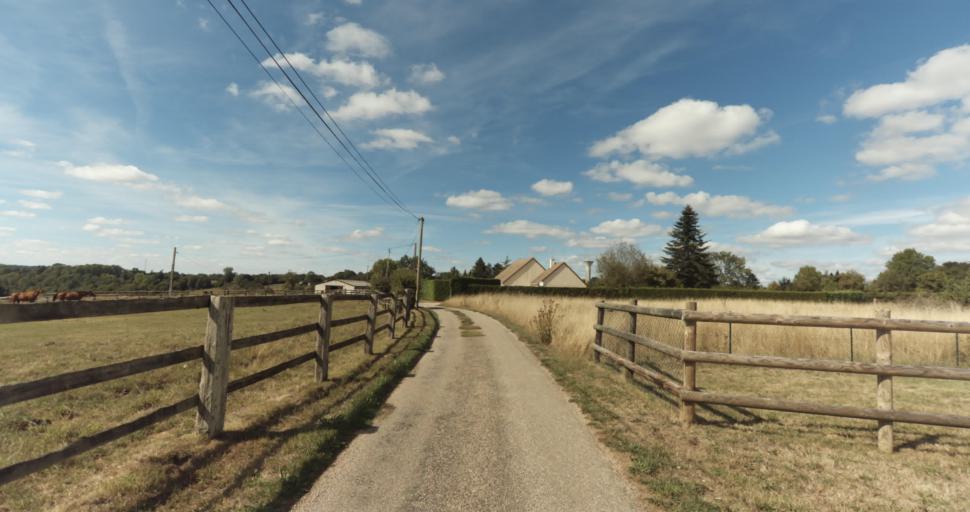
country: FR
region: Lower Normandy
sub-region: Departement de l'Orne
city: Vimoutiers
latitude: 48.9280
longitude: 0.2331
